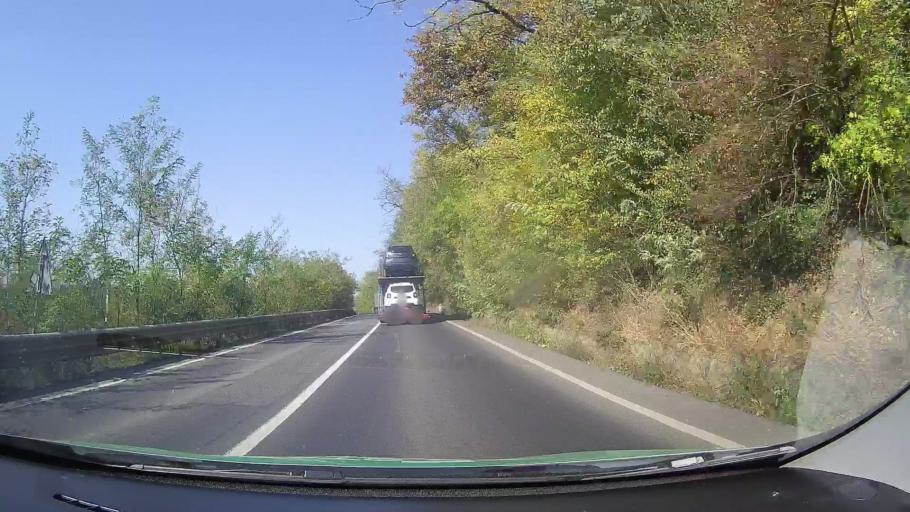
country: RO
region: Arad
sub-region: Comuna Bata
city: Bata
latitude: 46.0359
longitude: 22.0639
